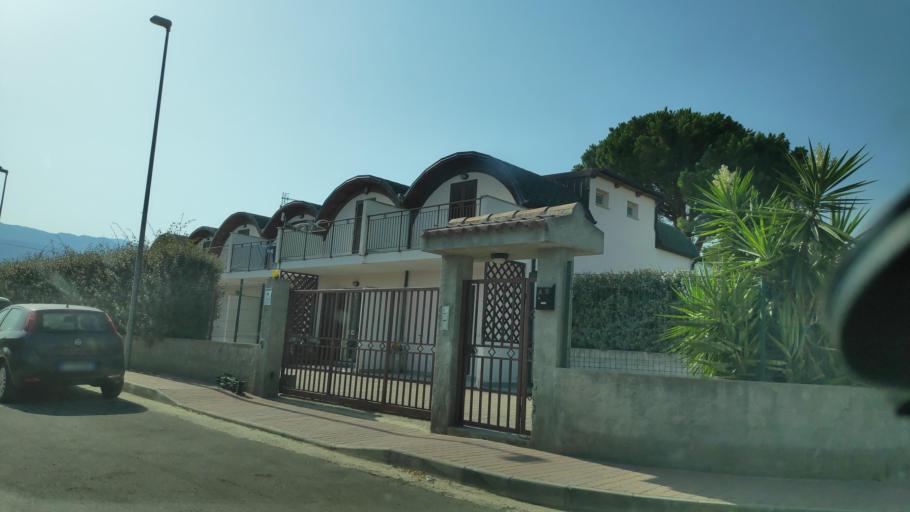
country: IT
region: Calabria
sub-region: Provincia di Catanzaro
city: Isca Marina
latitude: 38.6008
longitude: 16.5645
